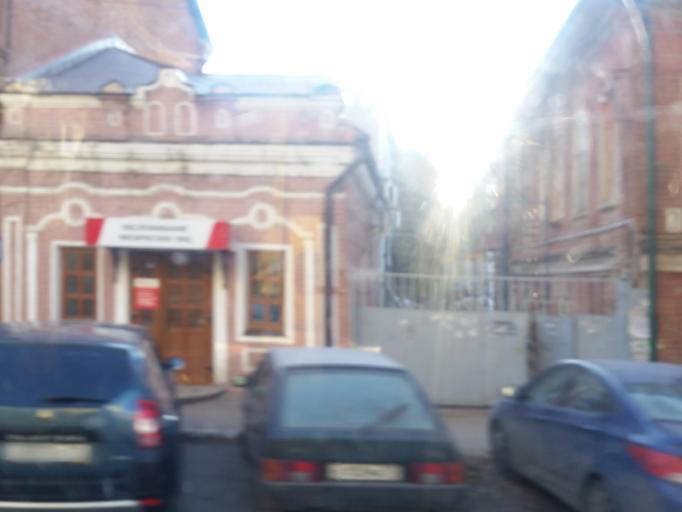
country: RU
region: Ulyanovsk
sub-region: Ulyanovskiy Rayon
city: Ulyanovsk
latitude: 54.3222
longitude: 48.3924
